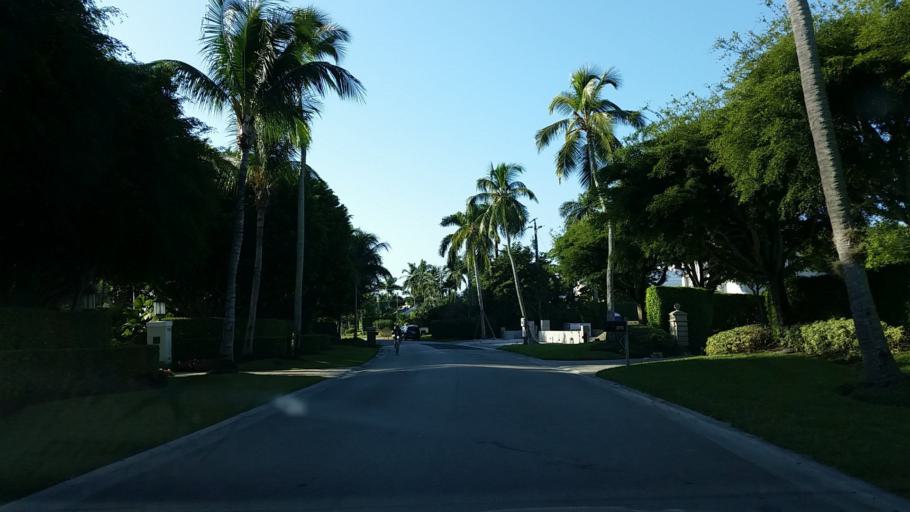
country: US
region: Florida
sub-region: Collier County
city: Naples
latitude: 26.1042
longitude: -81.7924
